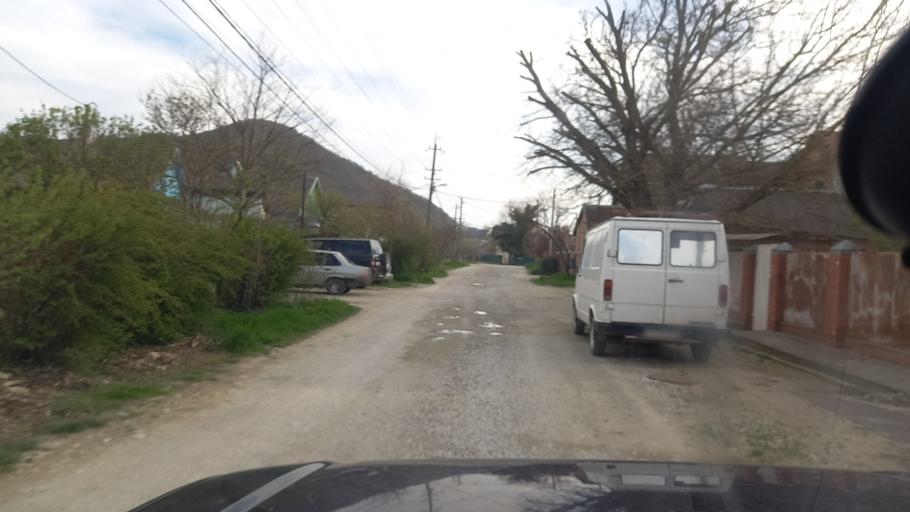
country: RU
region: Krasnodarskiy
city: Arkhipo-Osipovka
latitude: 44.3665
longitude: 38.5429
